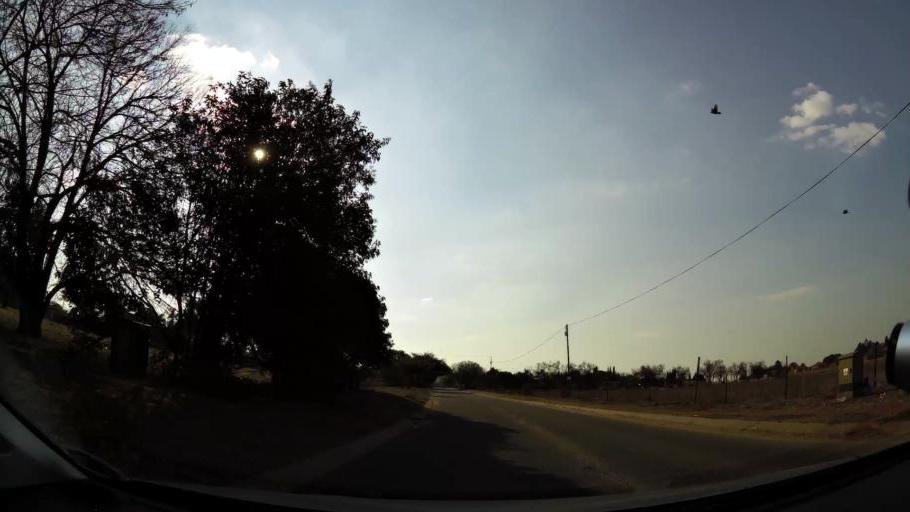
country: ZA
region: Gauteng
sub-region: City of Johannesburg Metropolitan Municipality
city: Modderfontein
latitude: -26.0787
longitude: 28.2018
